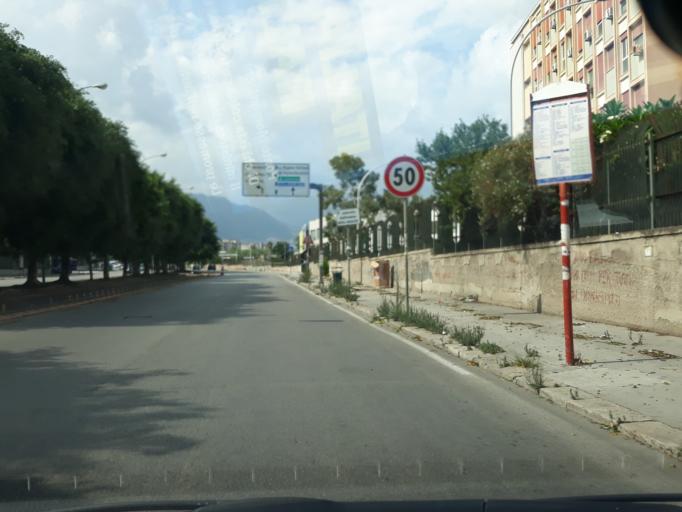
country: IT
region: Sicily
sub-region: Palermo
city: Palermo
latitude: 38.1029
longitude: 13.3489
